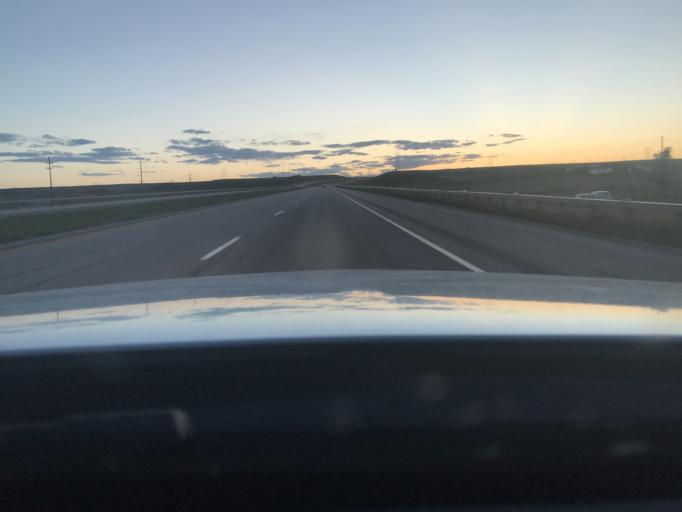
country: US
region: Wyoming
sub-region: Converse County
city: Glenrock
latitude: 42.8265
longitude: -105.8163
